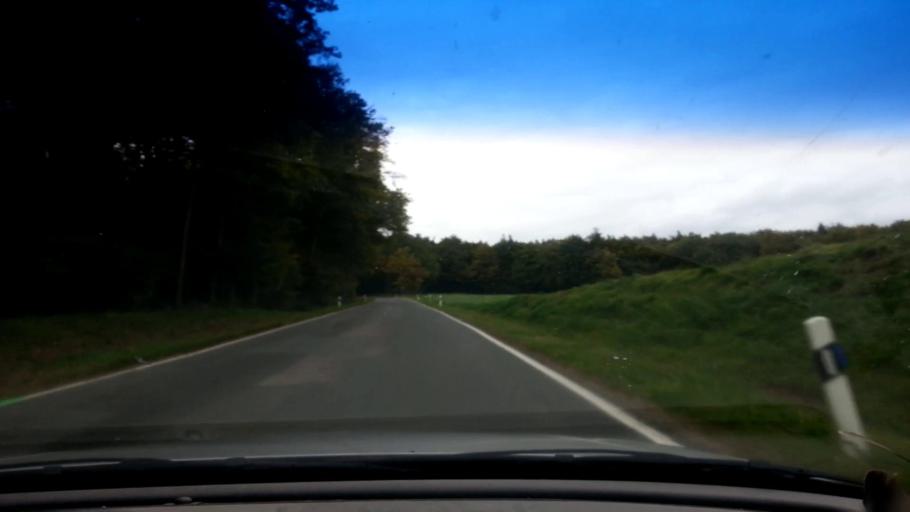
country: DE
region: Bavaria
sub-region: Upper Franconia
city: Priesendorf
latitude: 49.9177
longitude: 10.7168
